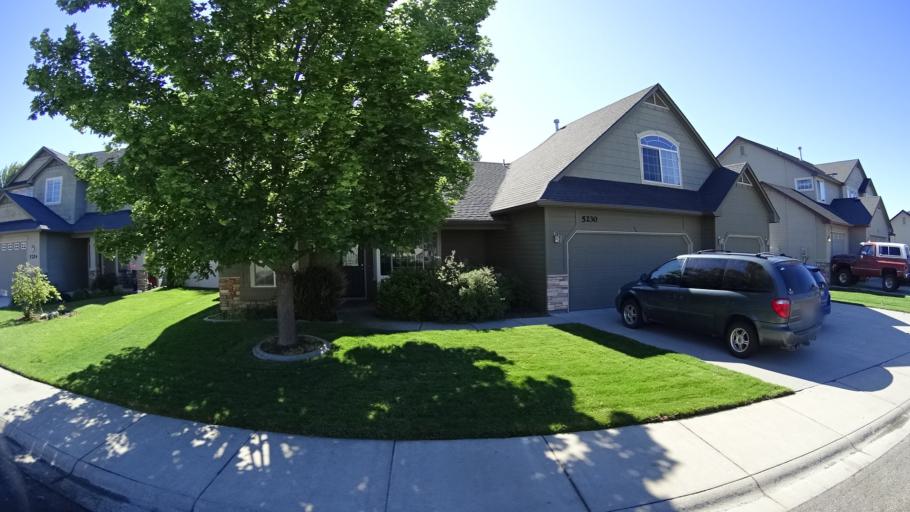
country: US
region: Idaho
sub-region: Ada County
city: Meridian
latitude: 43.6523
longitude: -116.4303
